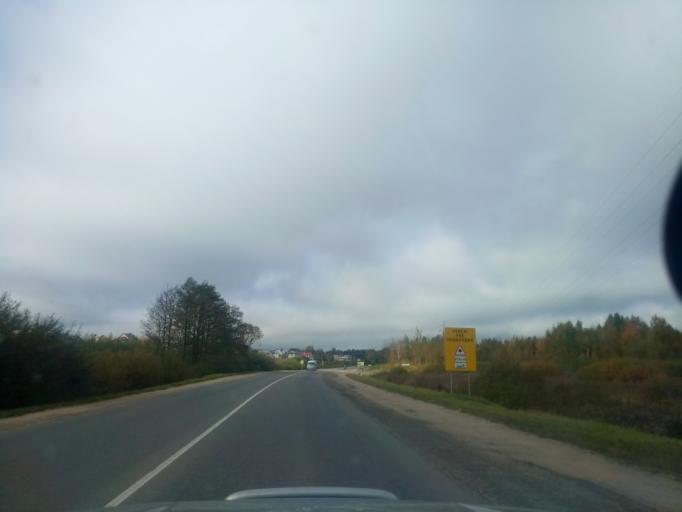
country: BY
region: Minsk
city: Zaslawye
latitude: 54.0017
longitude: 27.2726
